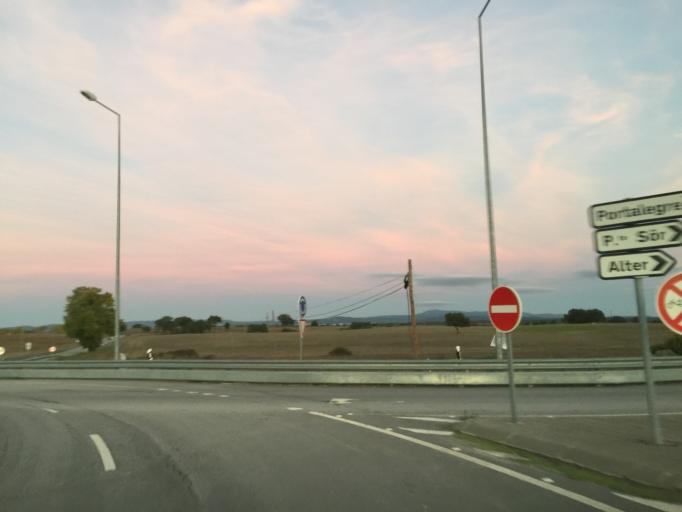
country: PT
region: Portalegre
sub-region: Alter do Chao
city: Alter do Chao
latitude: 39.2957
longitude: -7.6305
